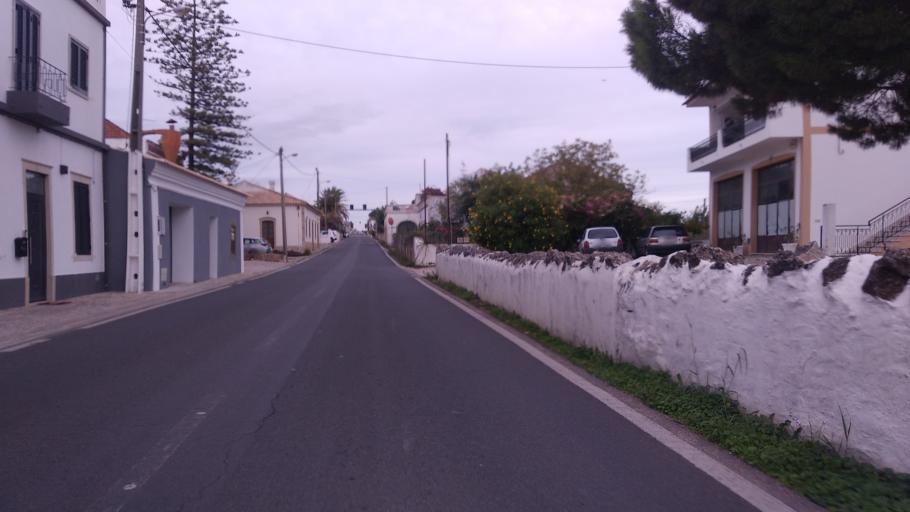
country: PT
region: Faro
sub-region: Sao Bras de Alportel
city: Sao Bras de Alportel
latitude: 37.1518
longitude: -7.9240
